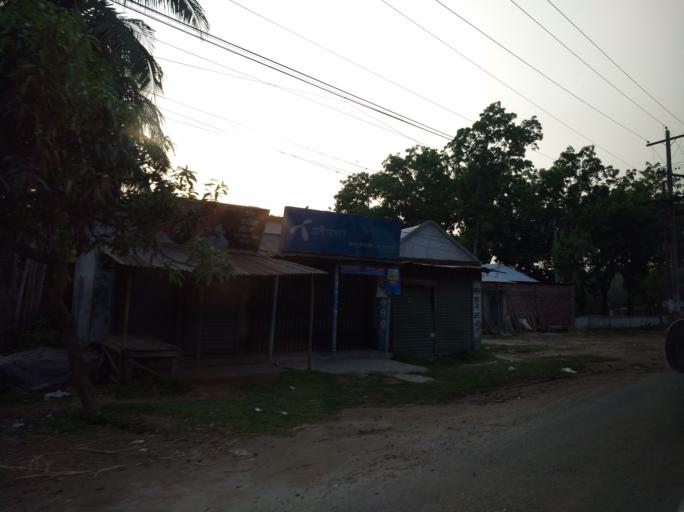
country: BD
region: Rajshahi
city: Bogra
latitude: 24.7045
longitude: 89.3978
